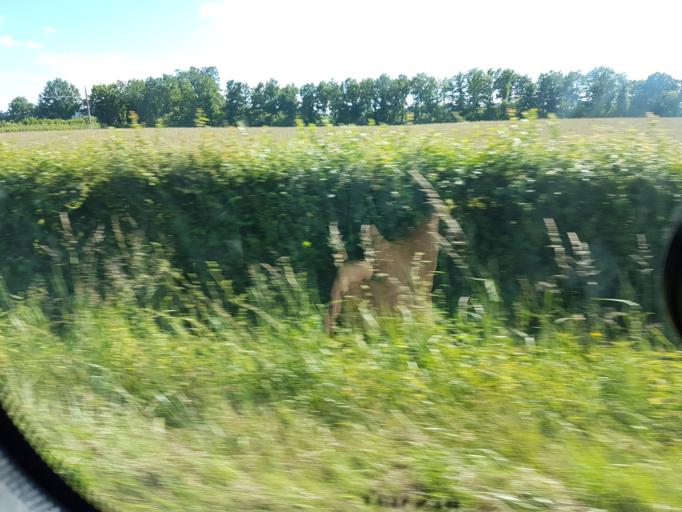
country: FR
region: Bourgogne
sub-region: Departement de Saone-et-Loire
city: Epinac
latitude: 47.0086
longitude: 4.4577
